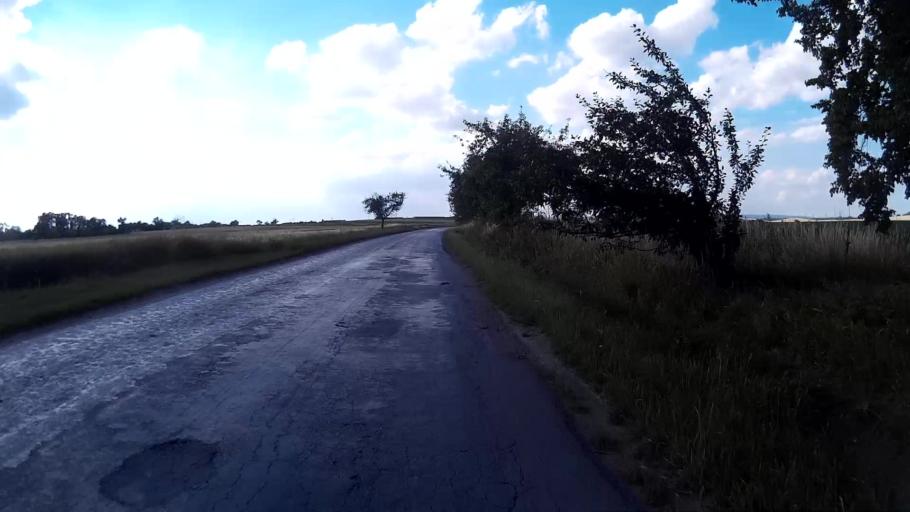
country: CZ
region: South Moravian
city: Tesany
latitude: 49.0442
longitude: 16.7734
